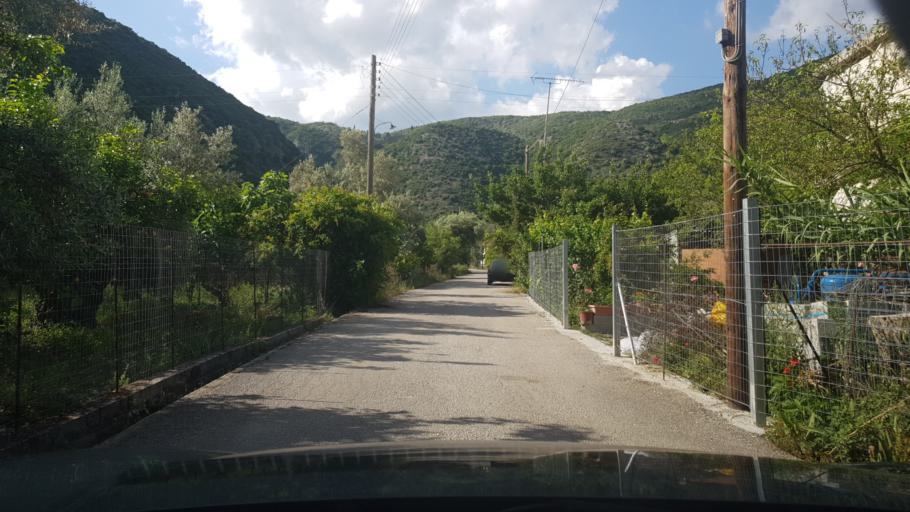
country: GR
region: Ionian Islands
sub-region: Lefkada
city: Nidri
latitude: 38.7166
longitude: 20.6956
